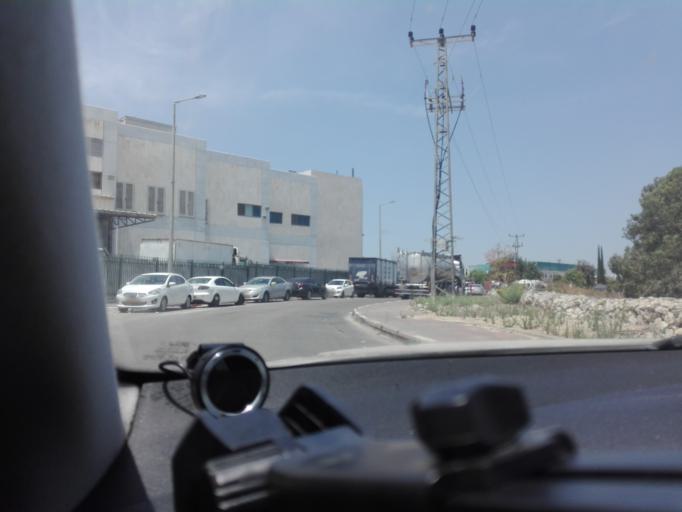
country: IL
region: Central District
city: Bene 'Ayish
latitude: 31.7394
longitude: 34.7501
